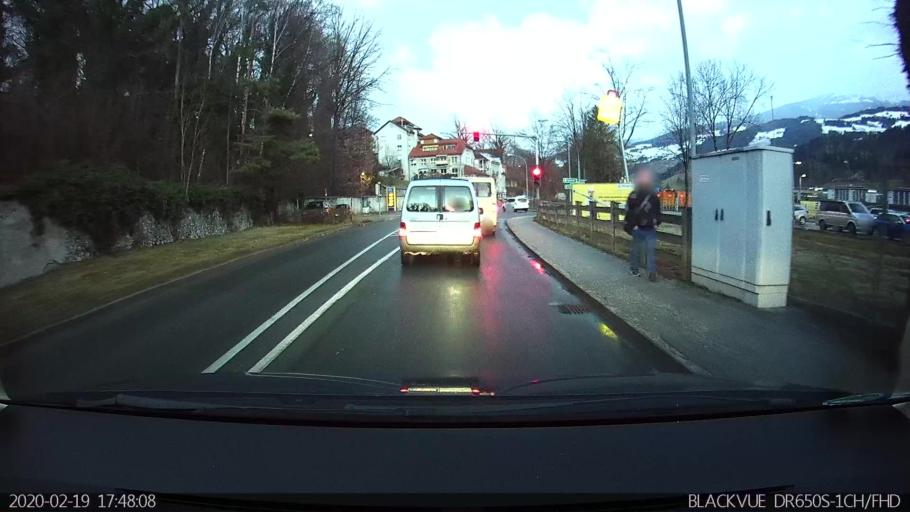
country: AT
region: Tyrol
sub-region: Politischer Bezirk Innsbruck Land
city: Hall in Tirol
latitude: 47.2807
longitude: 11.5113
